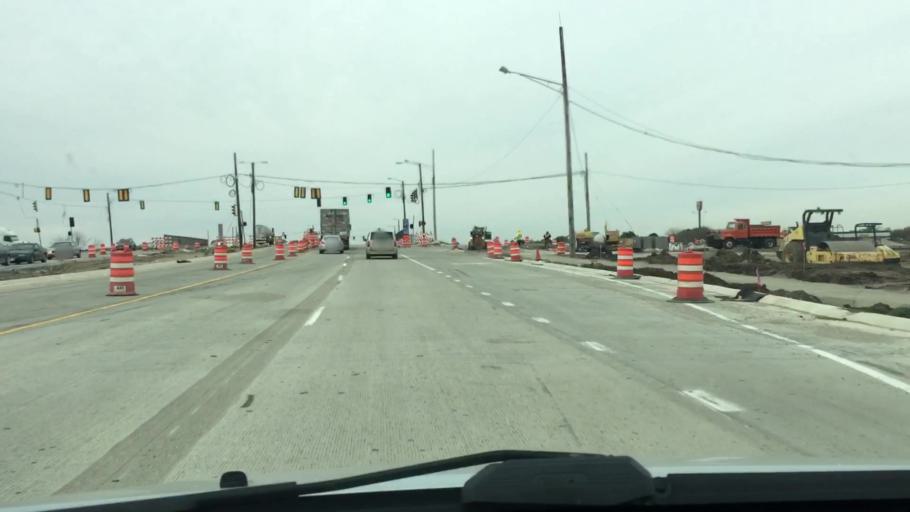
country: US
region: Wisconsin
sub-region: Racine County
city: Caledonia
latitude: 42.8727
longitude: -87.9347
